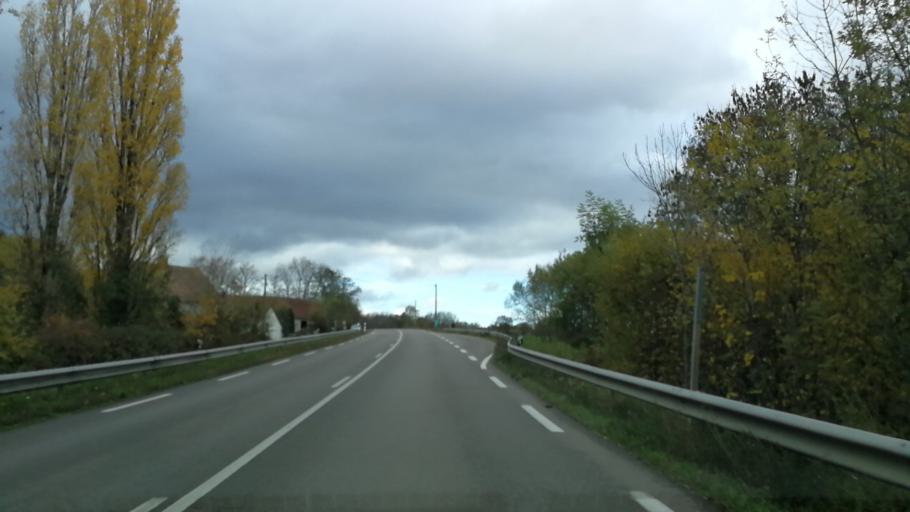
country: FR
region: Bourgogne
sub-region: Departement de la Cote-d'Or
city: Saulieu
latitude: 47.2706
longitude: 4.2530
